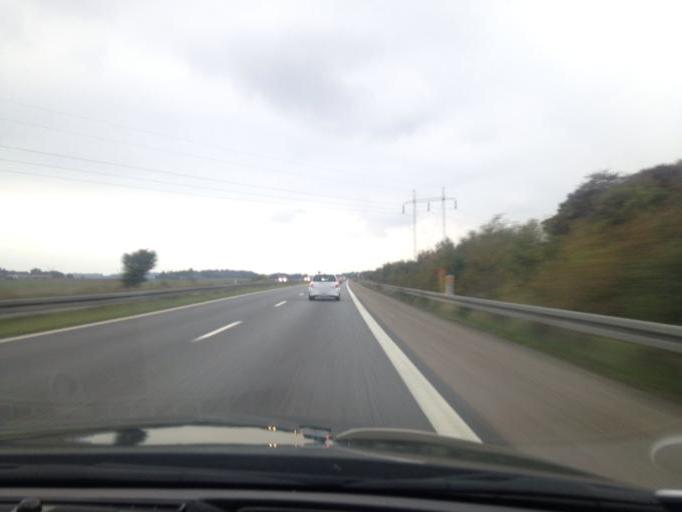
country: DK
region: South Denmark
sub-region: Kolding Kommune
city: Christiansfeld
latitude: 55.3212
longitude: 9.4367
